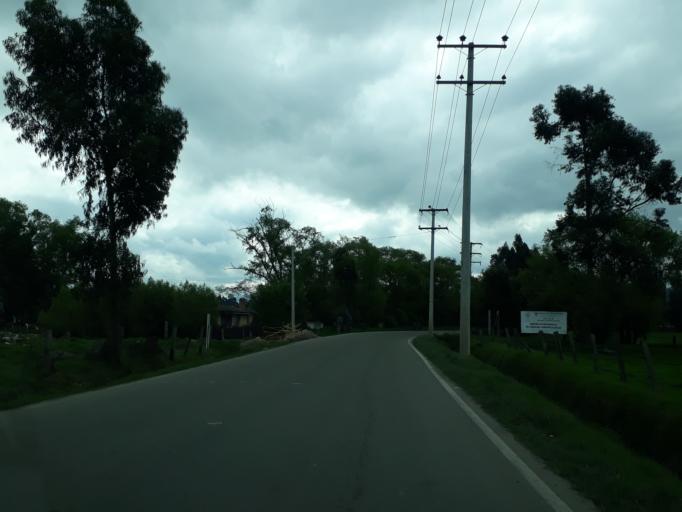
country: CO
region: Cundinamarca
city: Ubate
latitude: 5.3211
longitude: -73.7950
